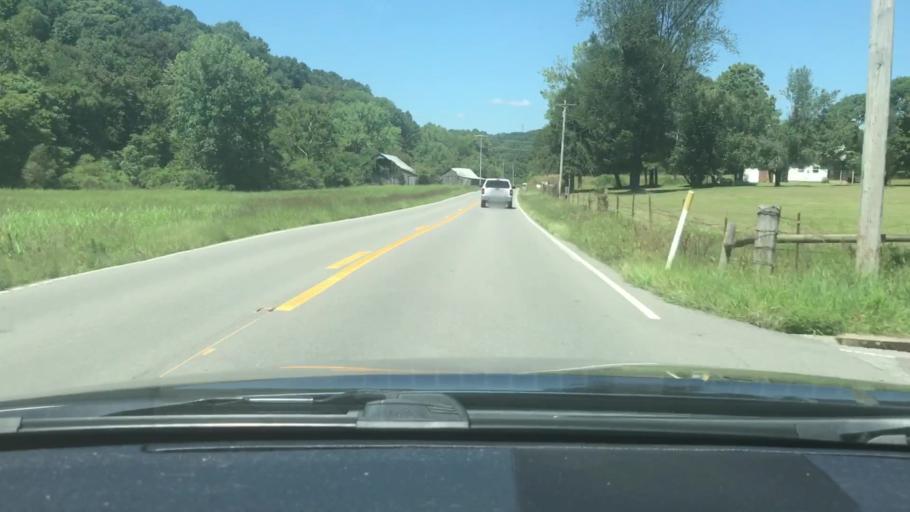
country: US
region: Tennessee
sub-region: Sumner County
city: White House
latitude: 36.4632
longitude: -86.5577
